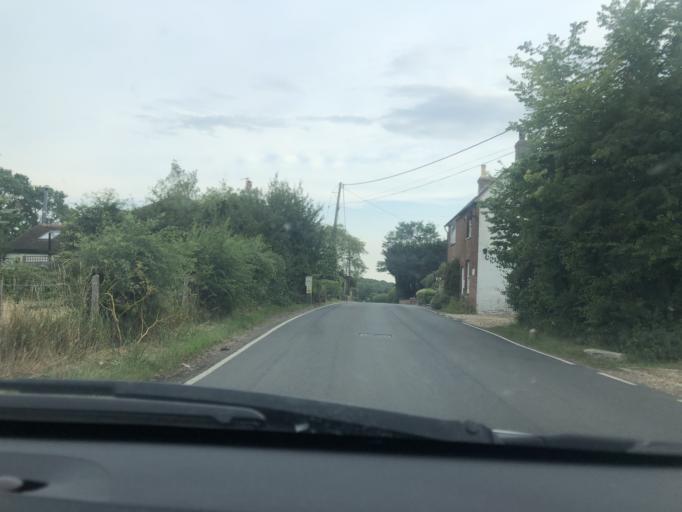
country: GB
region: England
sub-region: Kent
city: Sturry
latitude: 51.3332
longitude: 1.1540
